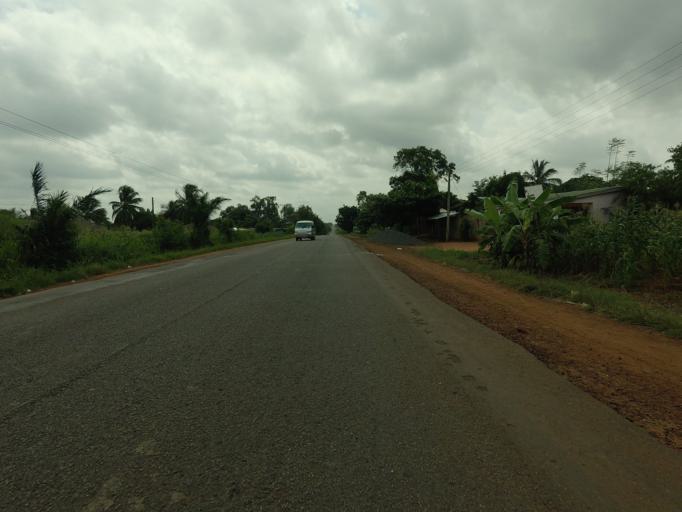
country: TG
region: Maritime
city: Lome
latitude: 6.1380
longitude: 1.1149
